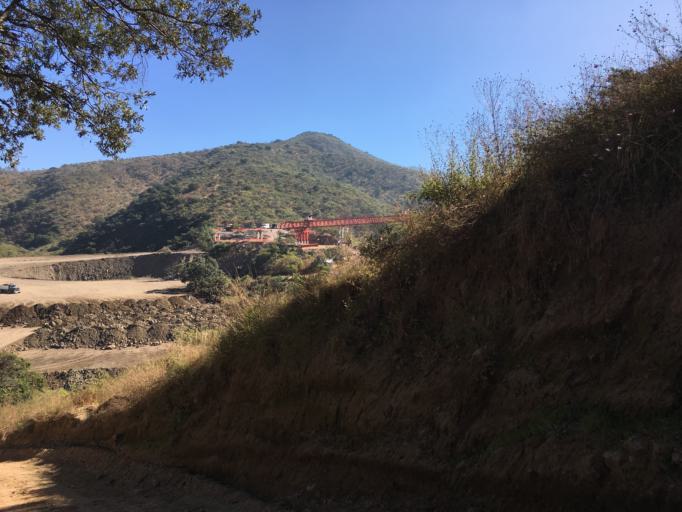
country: MX
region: Michoacan
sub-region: Morelia
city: Montana Monarca (Punta Altozano)
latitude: 19.6722
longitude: -101.1485
